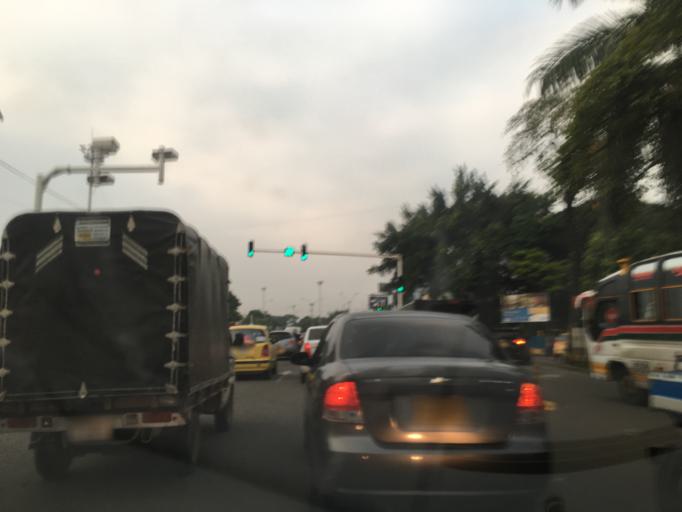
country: CO
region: Valle del Cauca
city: Cali
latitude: 3.4630
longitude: -76.5221
